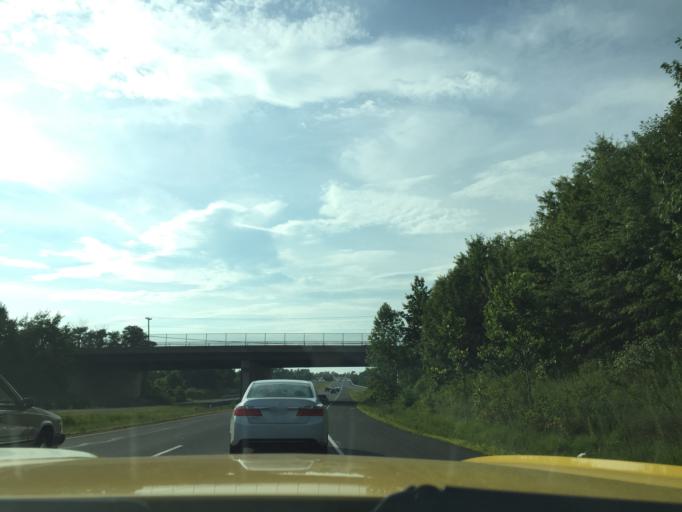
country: US
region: Virginia
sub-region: Fairfax County
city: Newington
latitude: 38.7239
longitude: -77.1822
